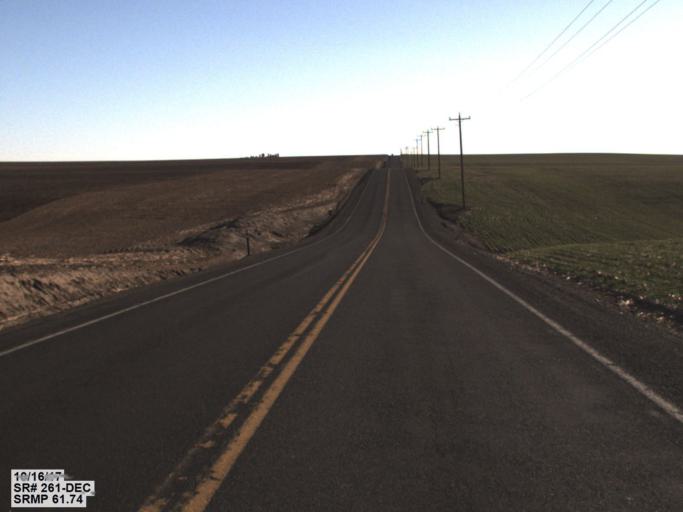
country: US
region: Washington
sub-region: Adams County
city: Ritzville
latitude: 47.1012
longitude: -118.3655
